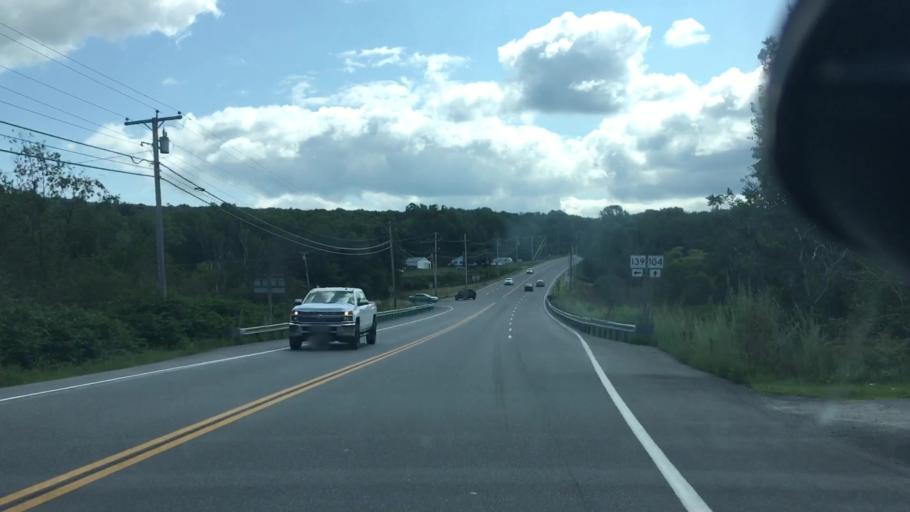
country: US
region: Maine
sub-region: Kennebec County
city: Waterville
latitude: 44.5996
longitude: -69.6561
